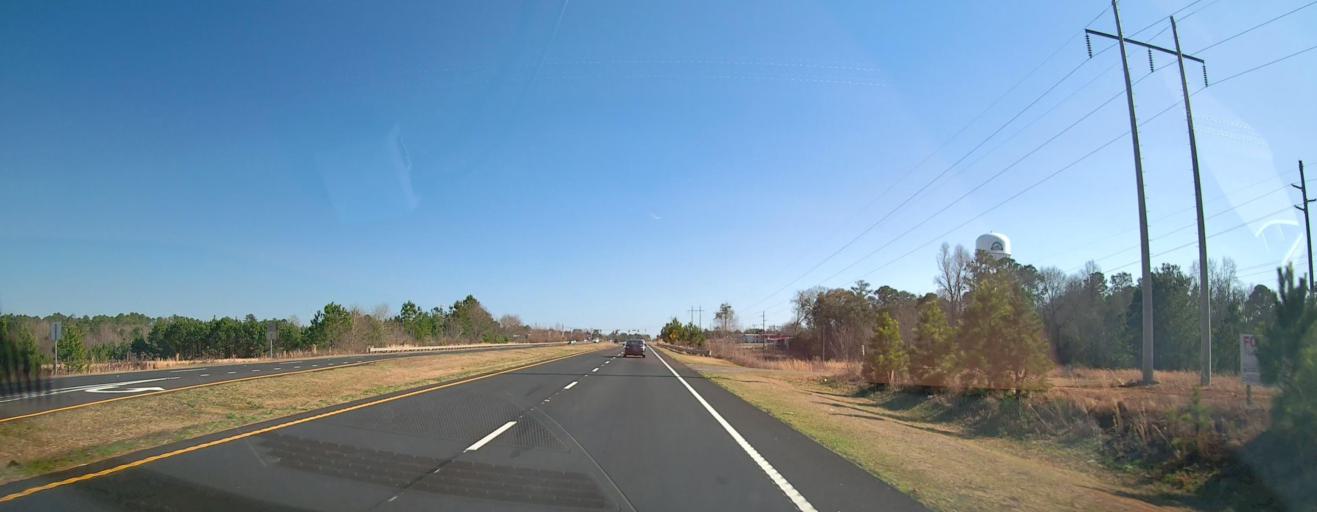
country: US
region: Georgia
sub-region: Sumter County
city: Americus
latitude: 32.0669
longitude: -84.2046
